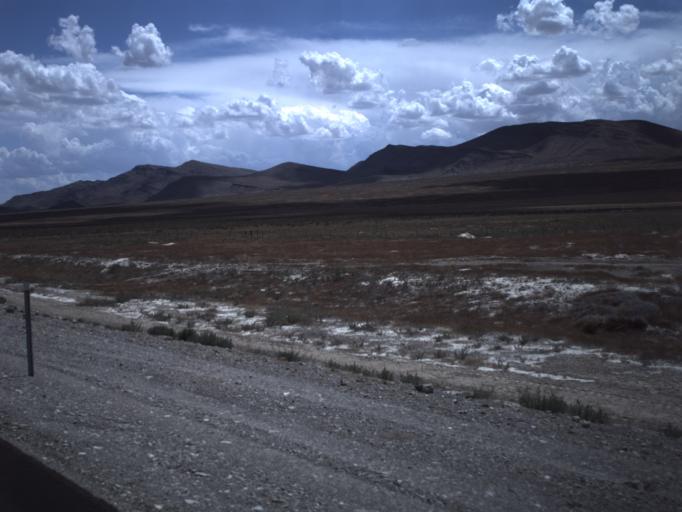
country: US
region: Utah
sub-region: Beaver County
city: Milford
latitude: 39.0825
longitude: -113.4934
